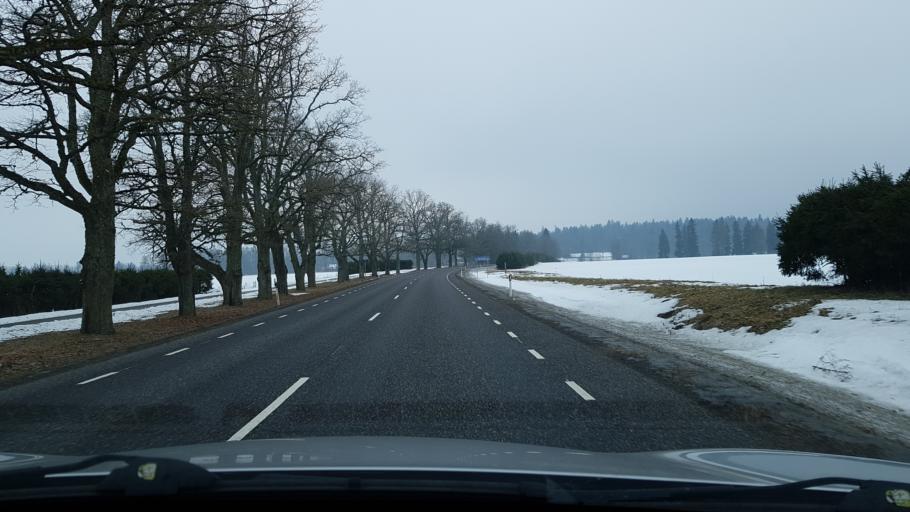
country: EE
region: Vorumaa
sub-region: Antsla vald
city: Vana-Antsla
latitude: 57.9071
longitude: 26.2916
